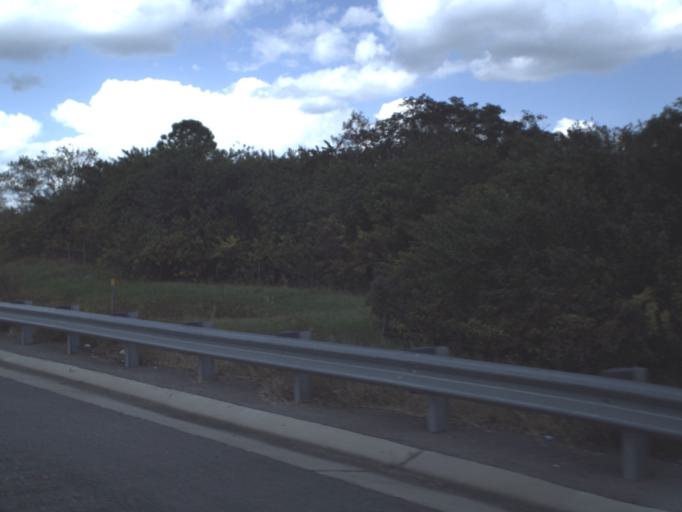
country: US
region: Florida
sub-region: Polk County
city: Fussels Corner
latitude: 28.0271
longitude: -81.8317
